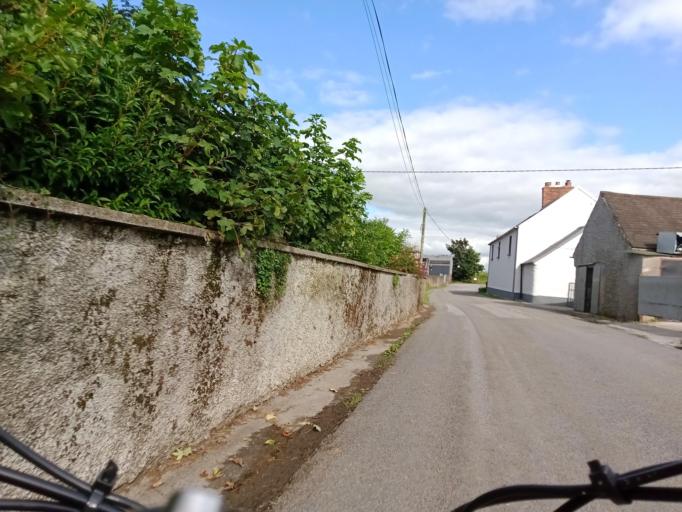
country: IE
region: Leinster
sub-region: Kilkenny
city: Kilkenny
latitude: 52.6037
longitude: -7.2374
